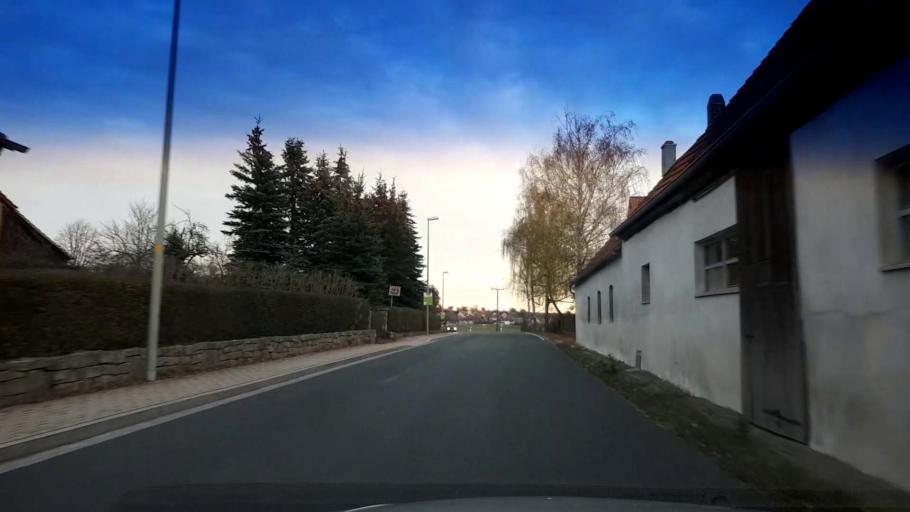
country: DE
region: Bavaria
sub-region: Upper Franconia
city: Priesendorf
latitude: 49.8872
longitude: 10.7494
